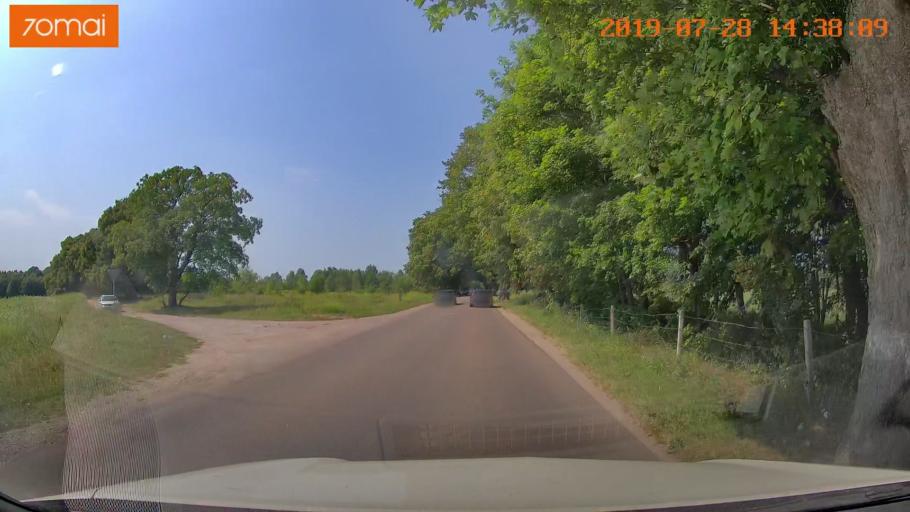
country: RU
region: Kaliningrad
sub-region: Gorod Kaliningrad
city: Yantarnyy
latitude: 54.8434
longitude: 19.9878
